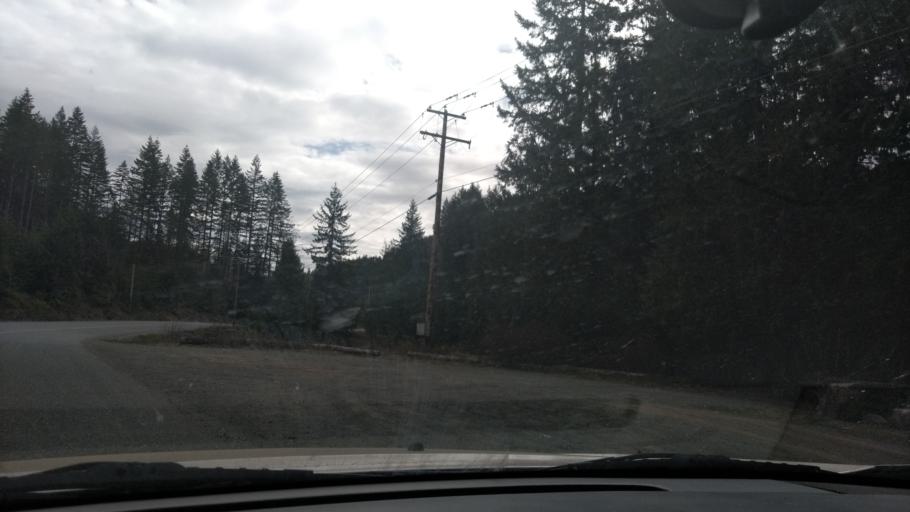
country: CA
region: British Columbia
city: Campbell River
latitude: 49.9951
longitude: -125.3810
